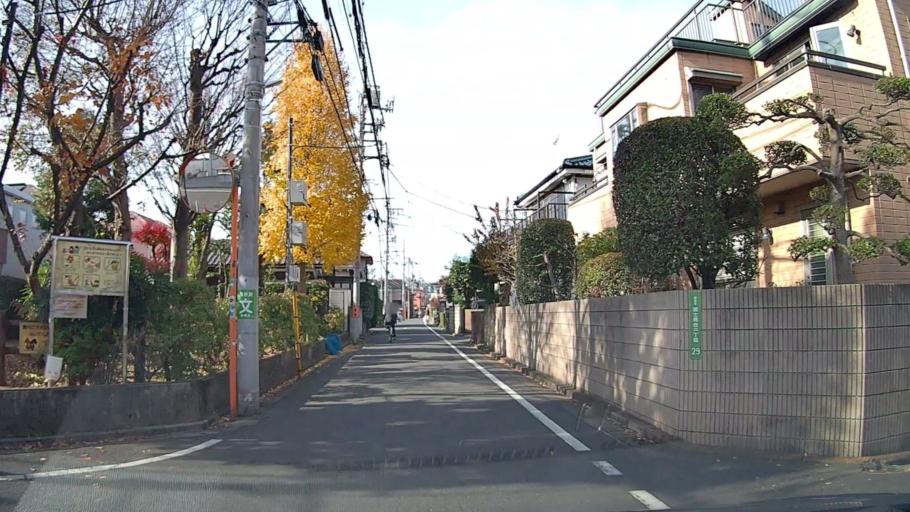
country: JP
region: Saitama
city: Wako
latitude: 35.7343
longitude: 139.6222
